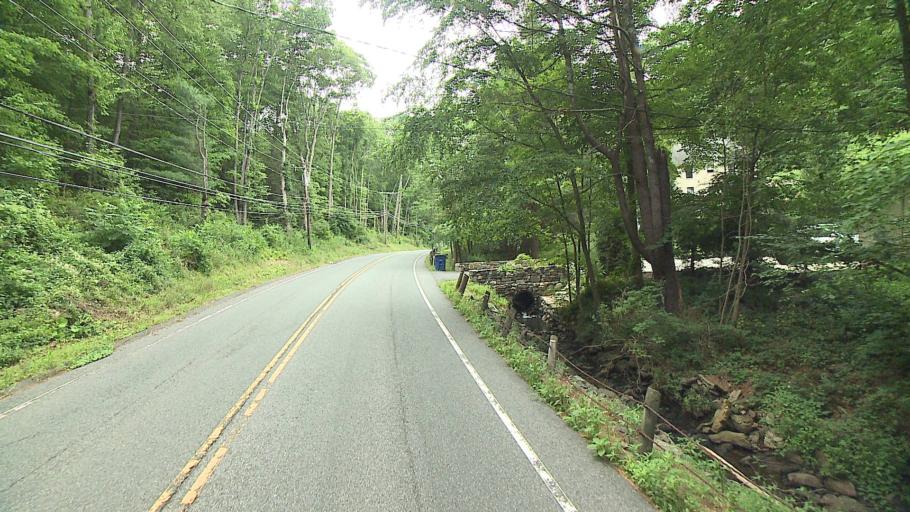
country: US
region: Connecticut
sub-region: Litchfield County
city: New Preston
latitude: 41.6230
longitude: -73.2985
